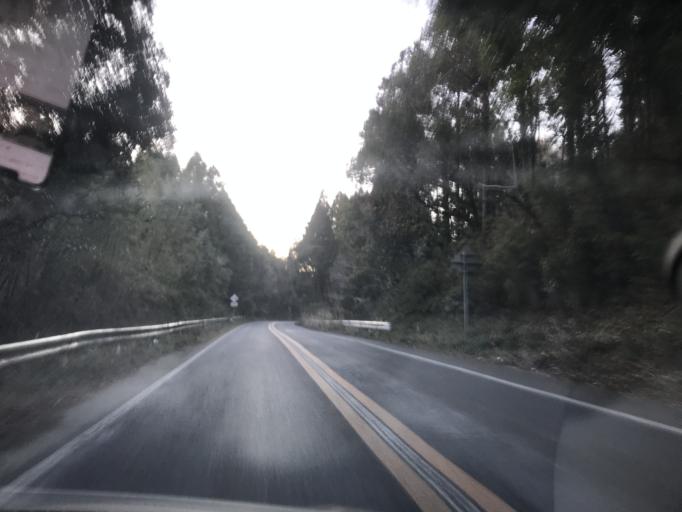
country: JP
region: Chiba
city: Sawara
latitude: 35.8230
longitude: 140.5129
